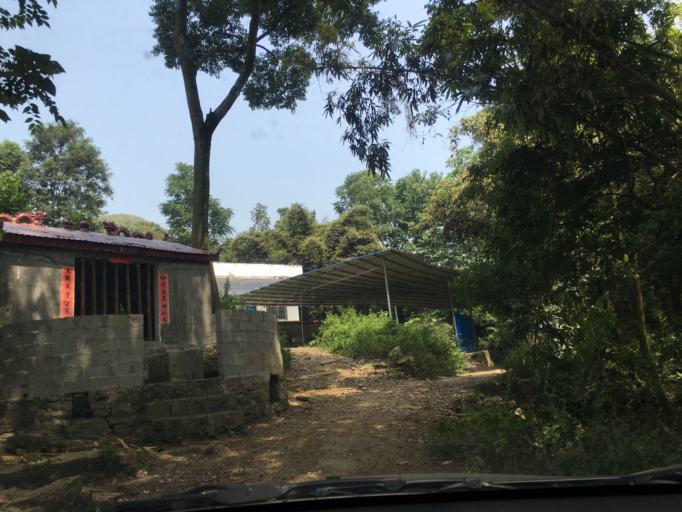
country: CN
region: Guizhou Sheng
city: Anshun
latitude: 25.5977
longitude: 105.6731
